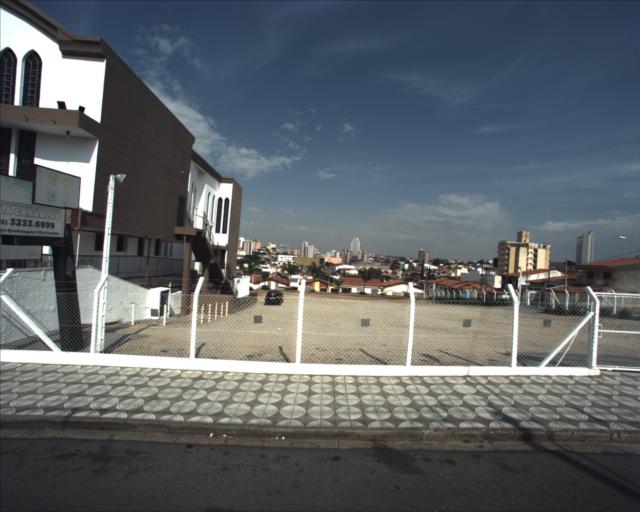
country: BR
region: Sao Paulo
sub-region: Sorocaba
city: Sorocaba
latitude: -23.4921
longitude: -47.4620
